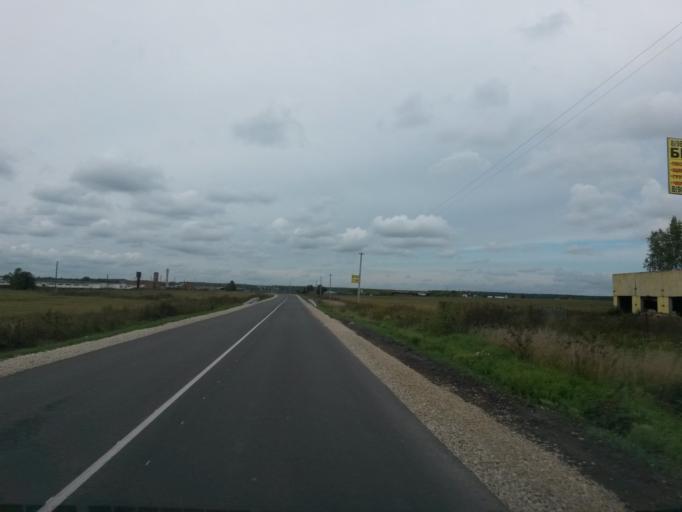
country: RU
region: Moskovskaya
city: Lyubuchany
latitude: 55.2481
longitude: 37.5670
